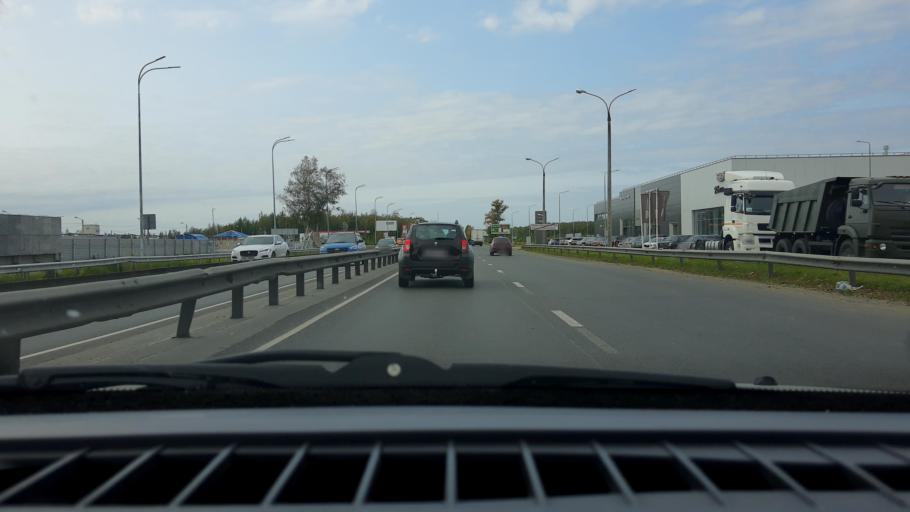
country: RU
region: Nizjnij Novgorod
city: Gorbatovka
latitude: 56.3088
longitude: 43.7920
